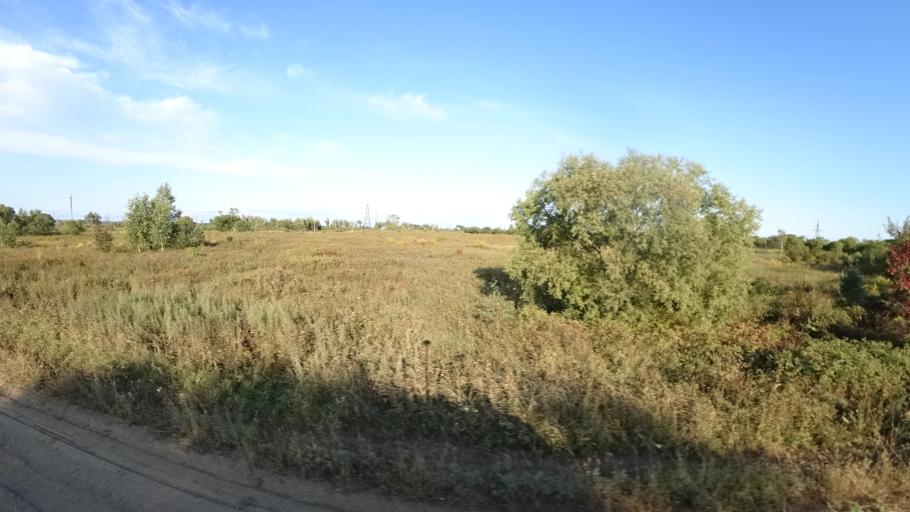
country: RU
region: Amur
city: Arkhara
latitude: 49.3673
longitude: 130.1360
